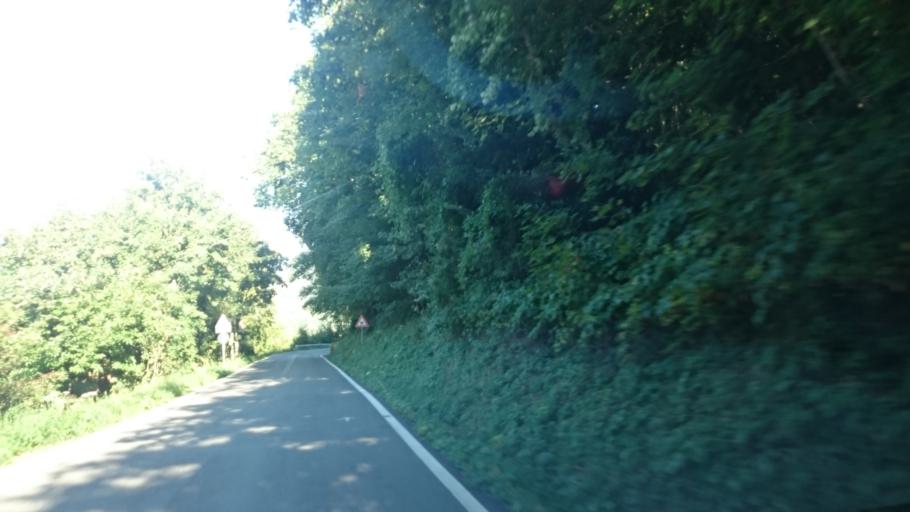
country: IT
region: Emilia-Romagna
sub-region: Provincia di Reggio Emilia
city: Villa Minozzo
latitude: 44.2995
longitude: 10.4441
